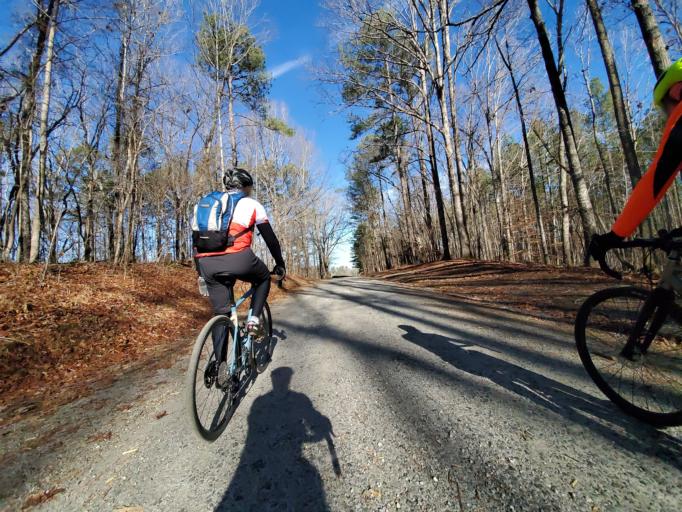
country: US
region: Georgia
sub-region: Fulton County
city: Chattahoochee Hills
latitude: 33.5644
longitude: -84.8077
